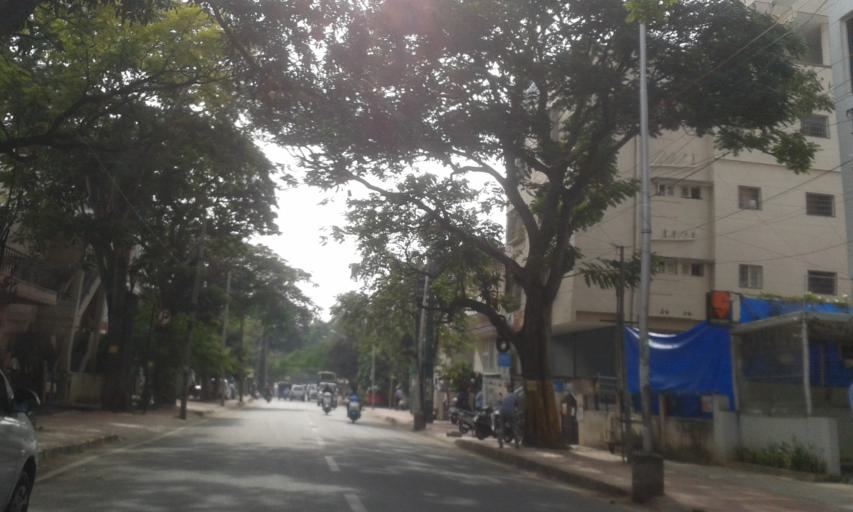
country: IN
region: Karnataka
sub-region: Bangalore Urban
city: Bangalore
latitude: 12.9336
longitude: 77.6270
